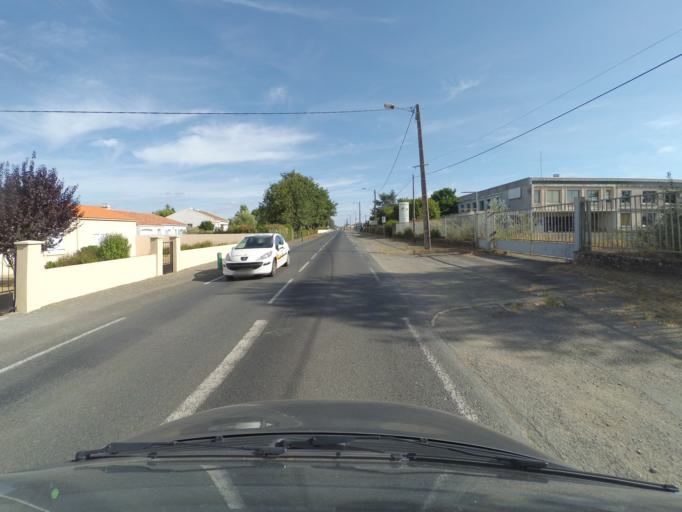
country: FR
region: Pays de la Loire
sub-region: Departement de la Loire-Atlantique
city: Vieillevigne
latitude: 46.9797
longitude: -1.4389
